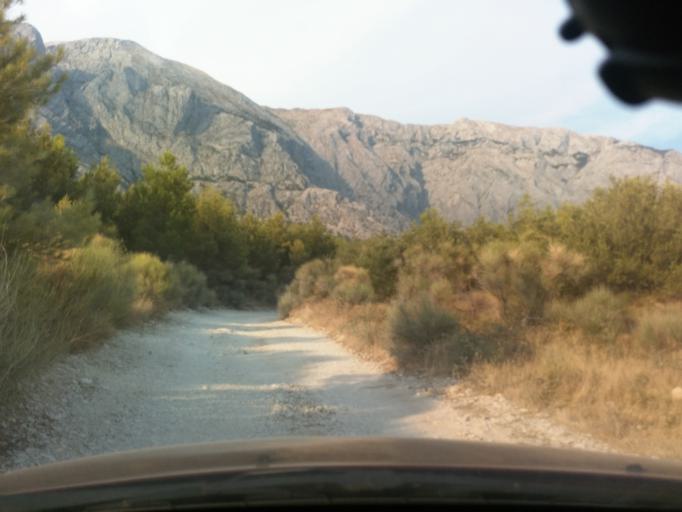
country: HR
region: Splitsko-Dalmatinska
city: Baska Voda
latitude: 43.3497
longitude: 16.9549
